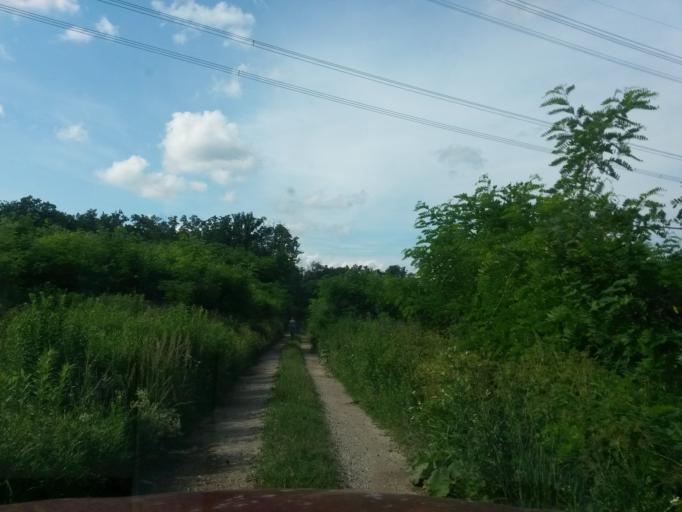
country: SK
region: Kosicky
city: Moldava nad Bodvou
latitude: 48.6094
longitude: 21.1134
